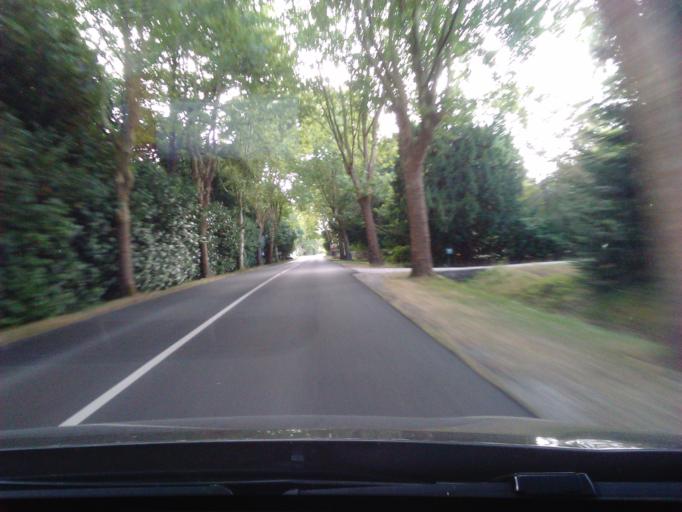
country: FR
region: Centre
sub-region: Departement du Loir-et-Cher
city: Cellettes
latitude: 47.5193
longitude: 1.3948
